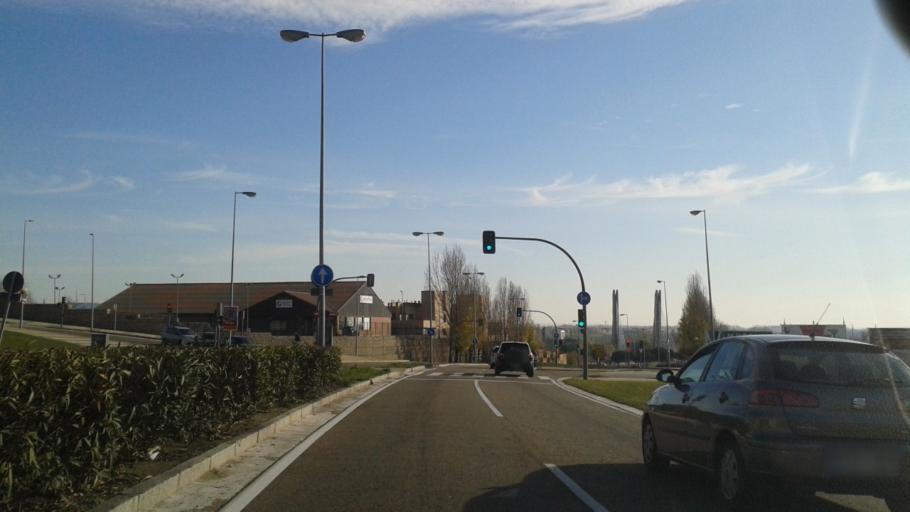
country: ES
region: Castille and Leon
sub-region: Provincia de Valladolid
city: Zaratan
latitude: 41.6303
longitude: -4.7615
